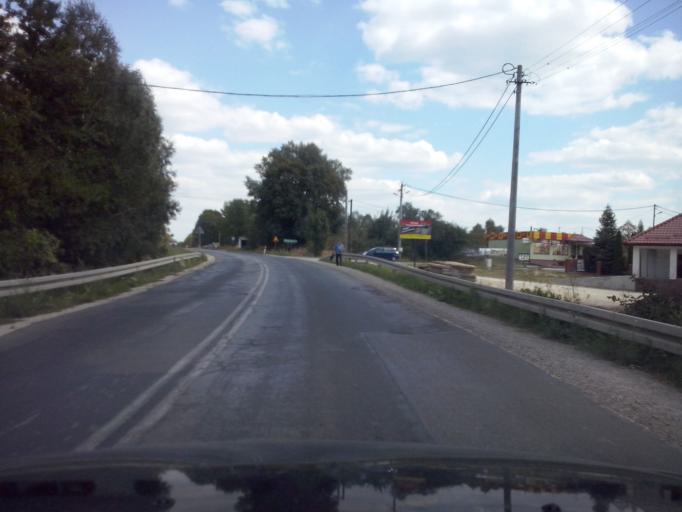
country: PL
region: Swietokrzyskie
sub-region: Powiat staszowski
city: Staszow
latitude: 50.5422
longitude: 21.1299
